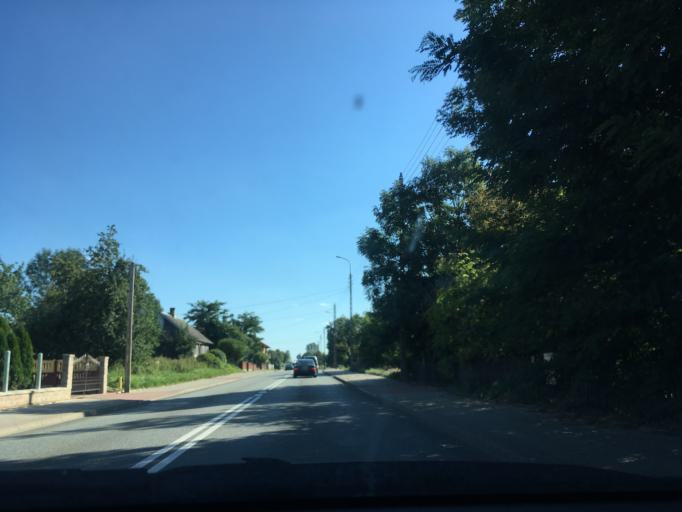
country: PL
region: Podlasie
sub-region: Powiat sokolski
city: Suchowola
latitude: 53.5004
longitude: 23.0972
